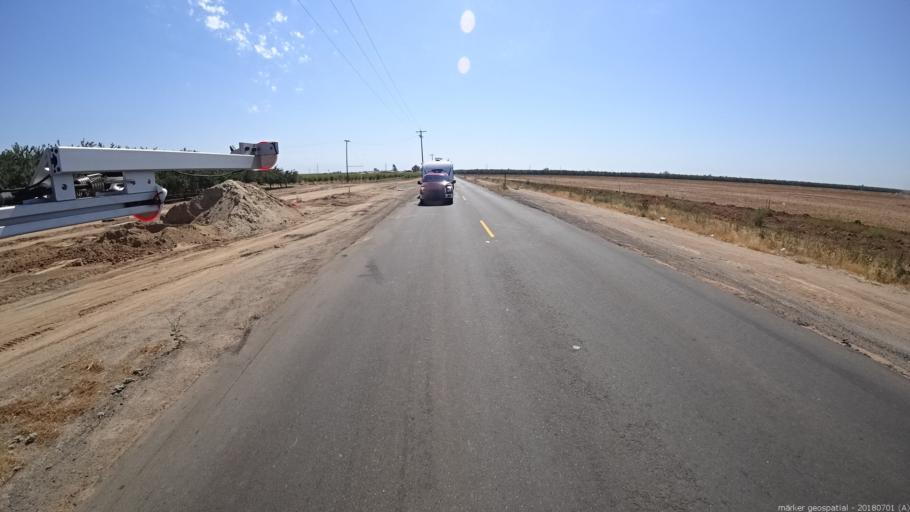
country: US
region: California
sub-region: Madera County
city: Parksdale
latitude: 36.8803
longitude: -119.9615
